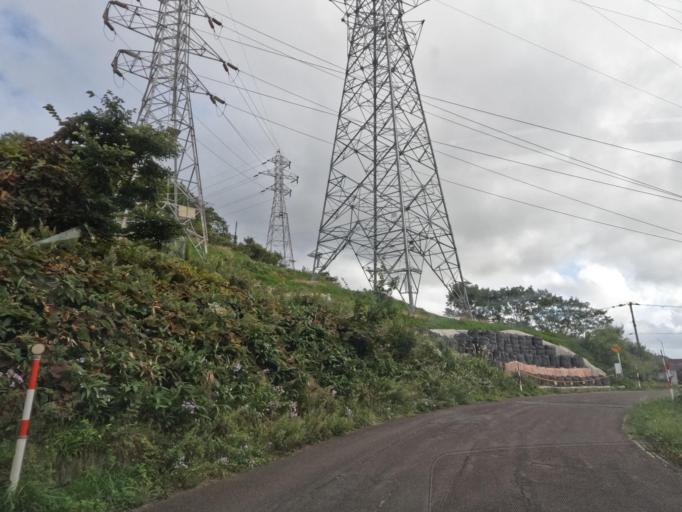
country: JP
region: Hokkaido
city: Muroran
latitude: 42.3274
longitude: 141.0017
